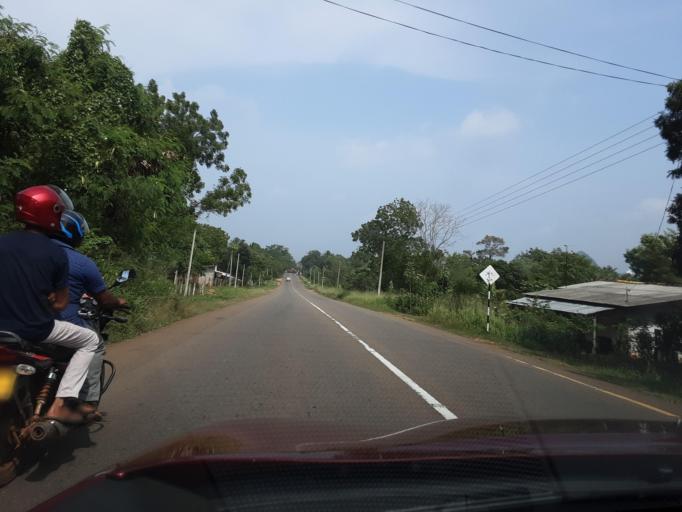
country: LK
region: North Central
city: Anuradhapura
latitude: 8.3268
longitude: 80.5010
